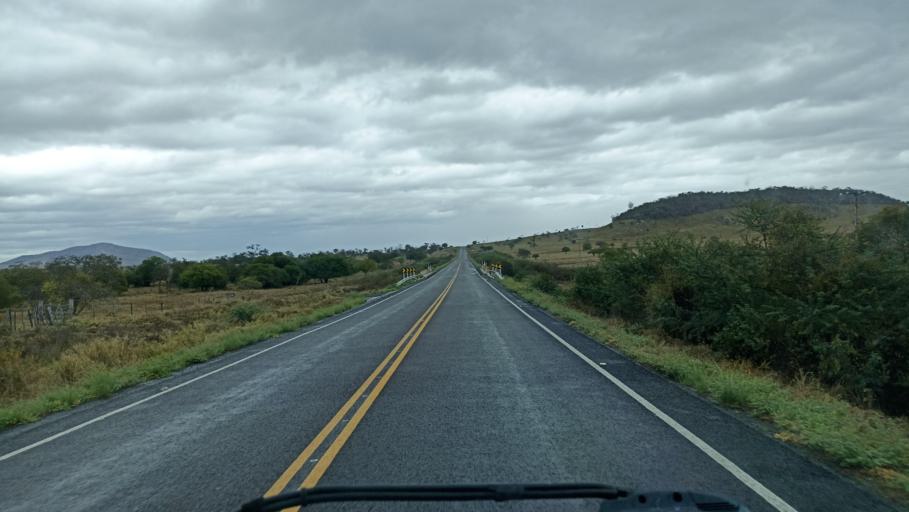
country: BR
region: Bahia
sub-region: Iacu
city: Iacu
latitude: -12.9626
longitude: -40.4823
